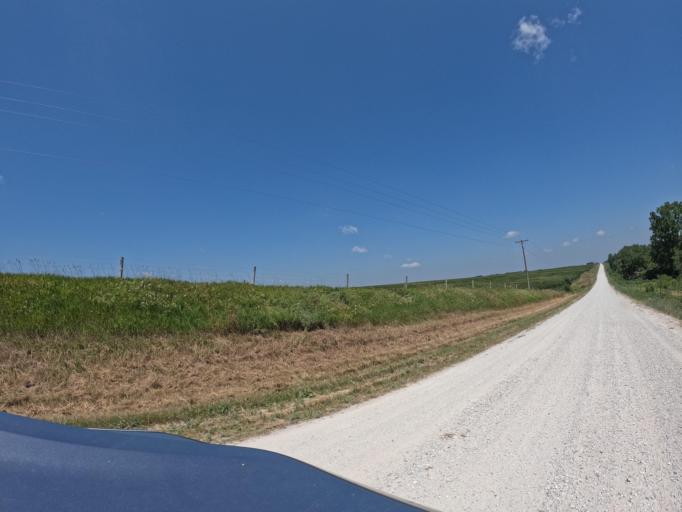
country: US
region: Iowa
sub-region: Keokuk County
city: Sigourney
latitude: 41.2694
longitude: -92.2381
